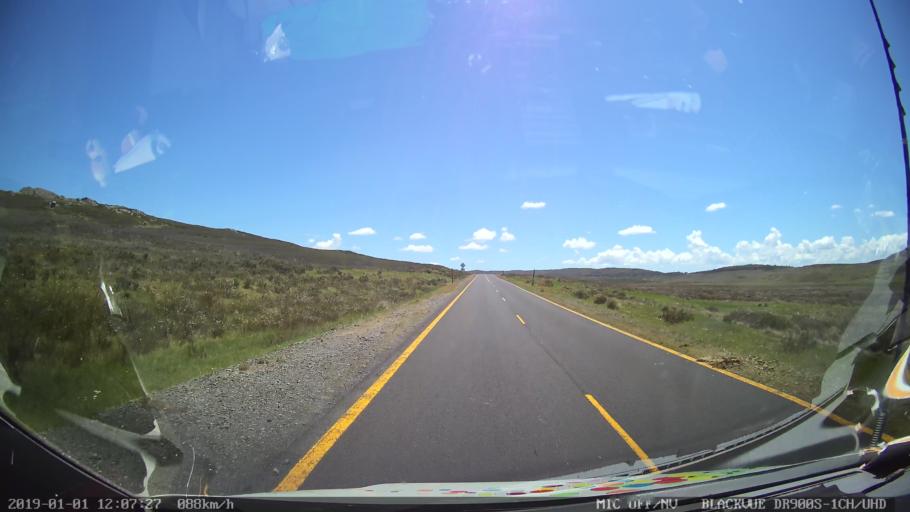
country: AU
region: New South Wales
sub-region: Tumut Shire
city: Tumut
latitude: -35.8326
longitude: 148.4897
